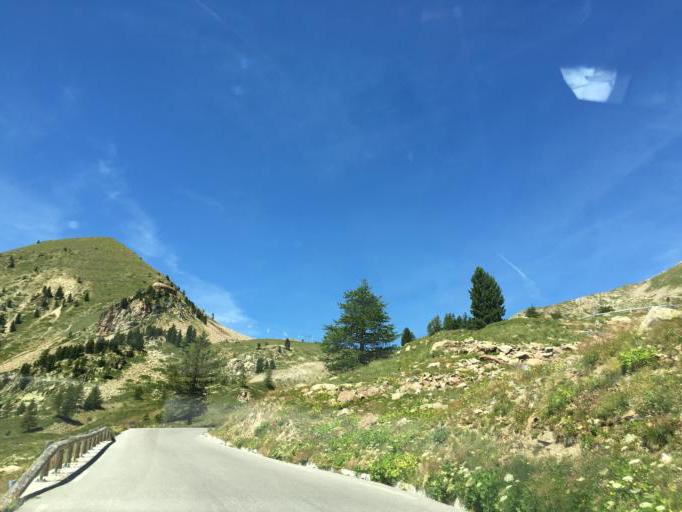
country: IT
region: Piedmont
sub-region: Provincia di Cuneo
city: Vinadio
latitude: 44.1958
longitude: 7.1553
